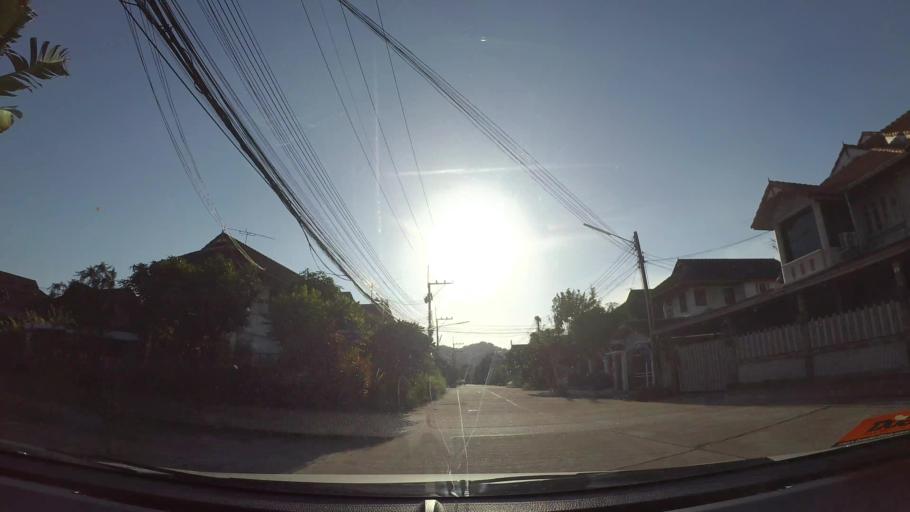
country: TH
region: Chon Buri
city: Si Racha
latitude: 13.1392
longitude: 100.9366
